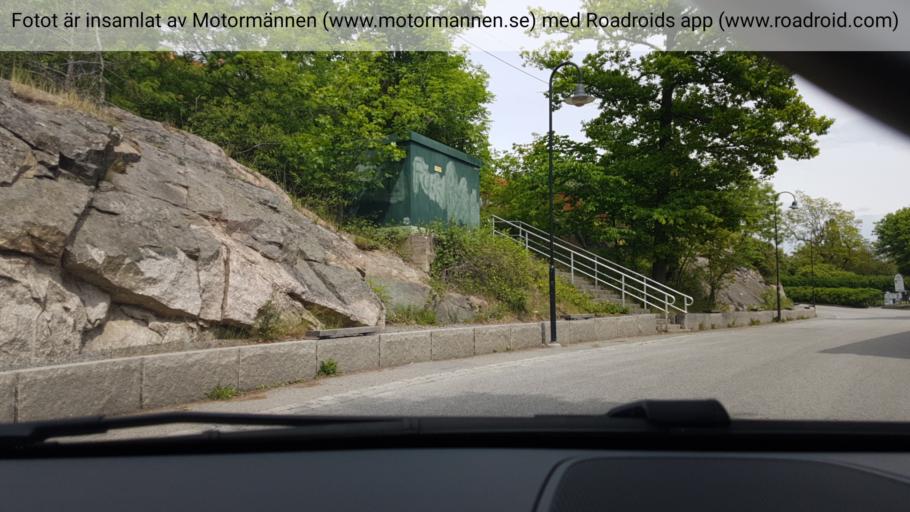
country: SE
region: Stockholm
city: Dalaro
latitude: 59.1306
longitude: 18.4056
